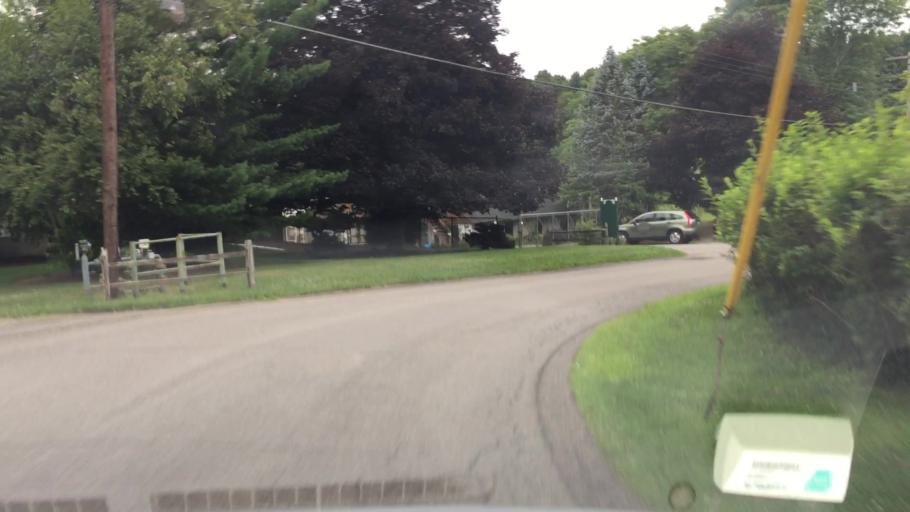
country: US
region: Pennsylvania
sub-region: Allegheny County
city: Allison Park
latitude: 40.5748
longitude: -79.9184
